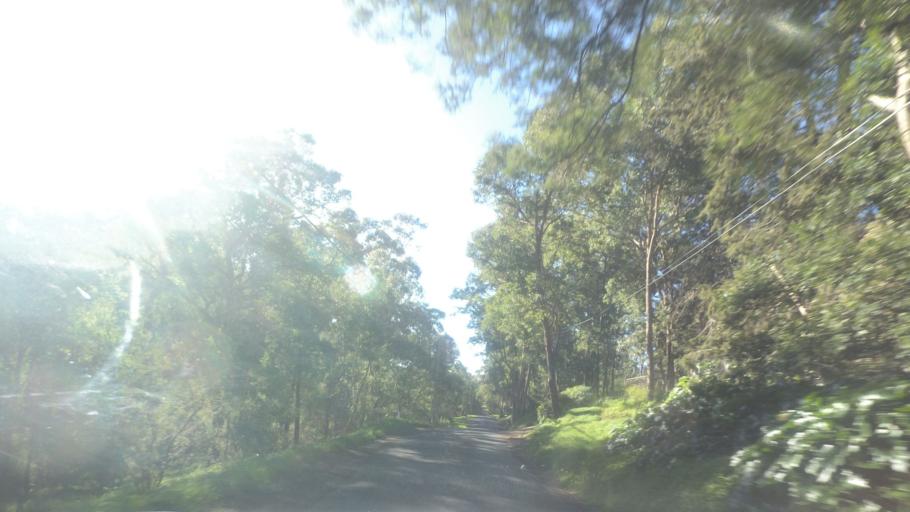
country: AU
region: Victoria
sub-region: Nillumbik
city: North Warrandyte
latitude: -37.7233
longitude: 145.2137
